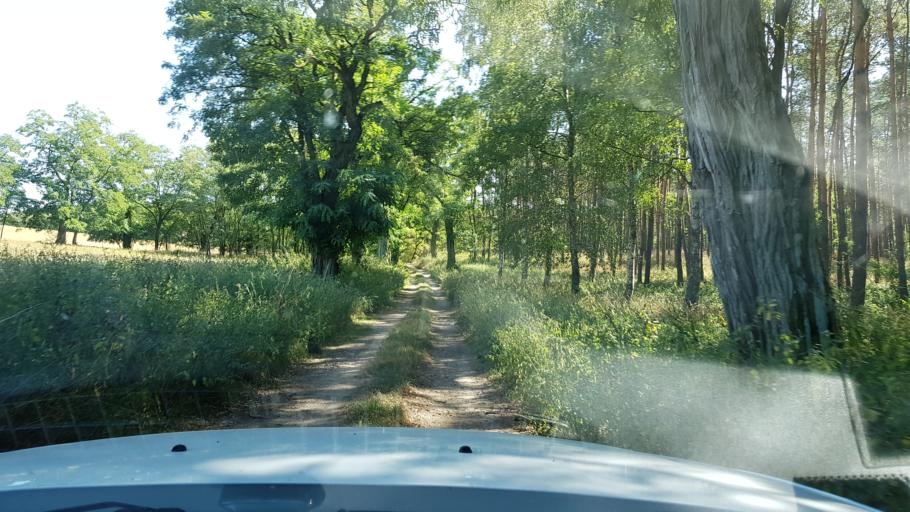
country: PL
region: West Pomeranian Voivodeship
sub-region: Powiat gryfinski
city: Cedynia
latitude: 52.8431
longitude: 14.2531
